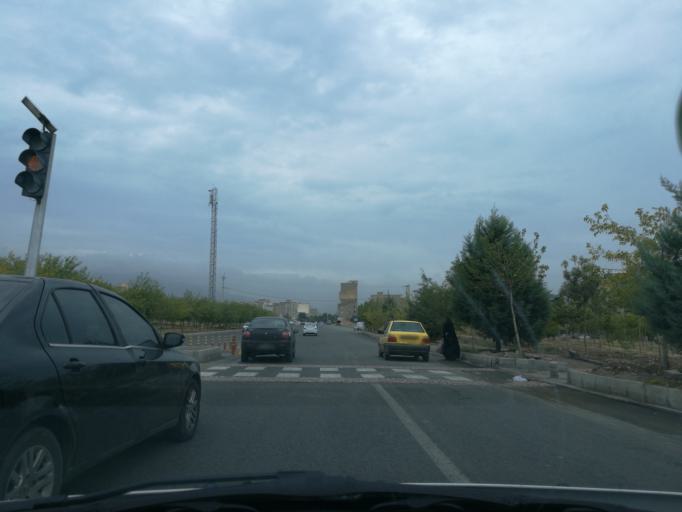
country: IR
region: Alborz
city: Karaj
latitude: 35.8626
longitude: 50.9335
